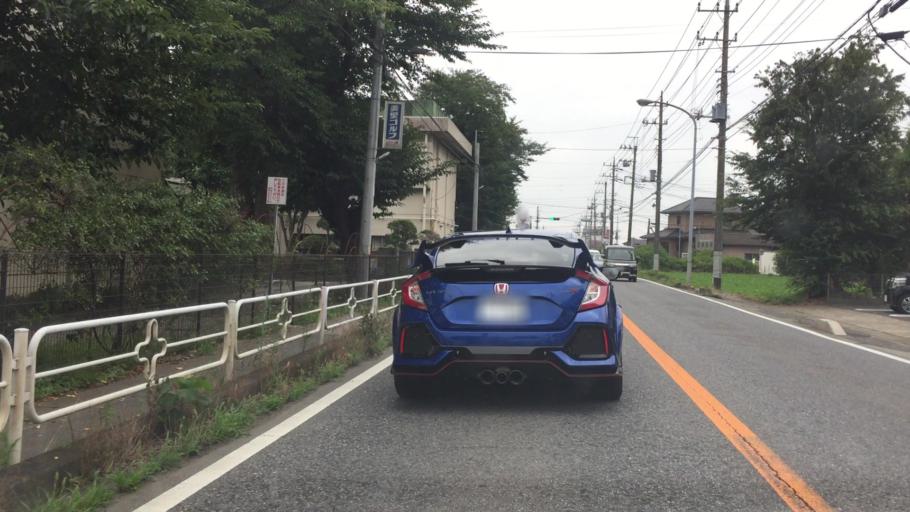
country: JP
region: Chiba
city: Abiko
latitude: 35.8316
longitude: 140.0036
